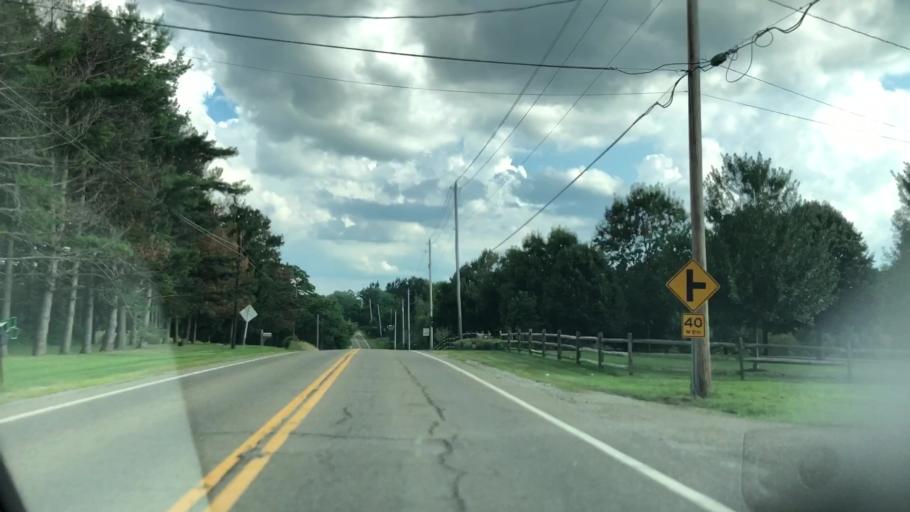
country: US
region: Ohio
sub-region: Summit County
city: Norton
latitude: 41.0669
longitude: -81.6389
